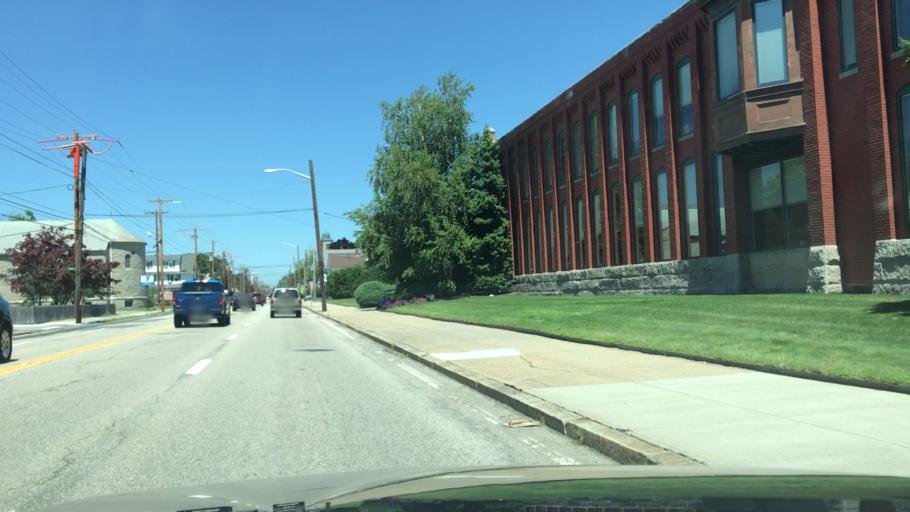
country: US
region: Massachusetts
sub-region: Bristol County
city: North Seekonk
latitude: 41.8825
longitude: -71.3539
